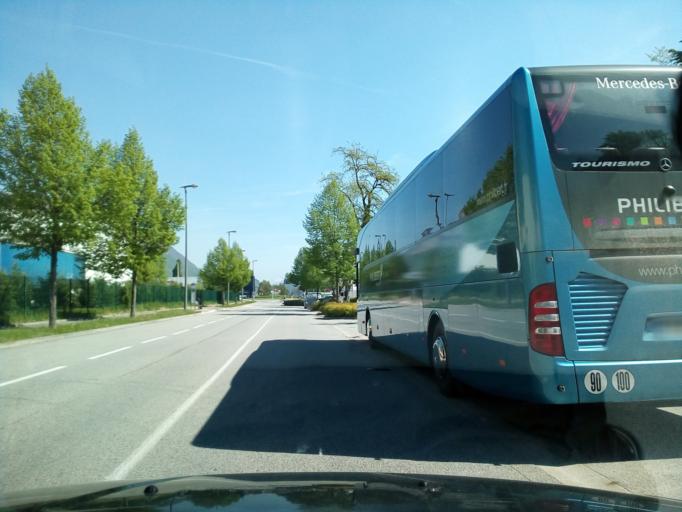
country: FR
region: Rhone-Alpes
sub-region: Departement de l'Isere
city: Crolles
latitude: 45.2706
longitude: 5.8872
